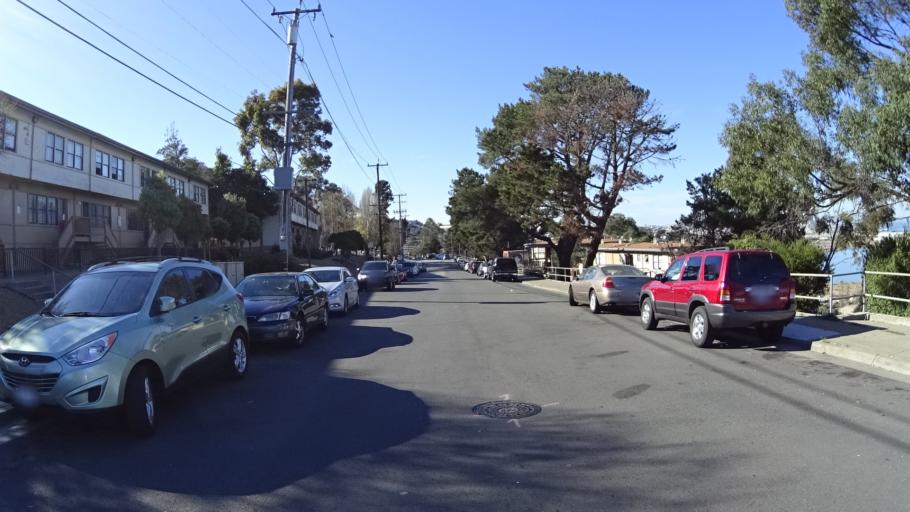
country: US
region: California
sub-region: San Mateo County
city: Brisbane
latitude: 37.7295
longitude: -122.3730
